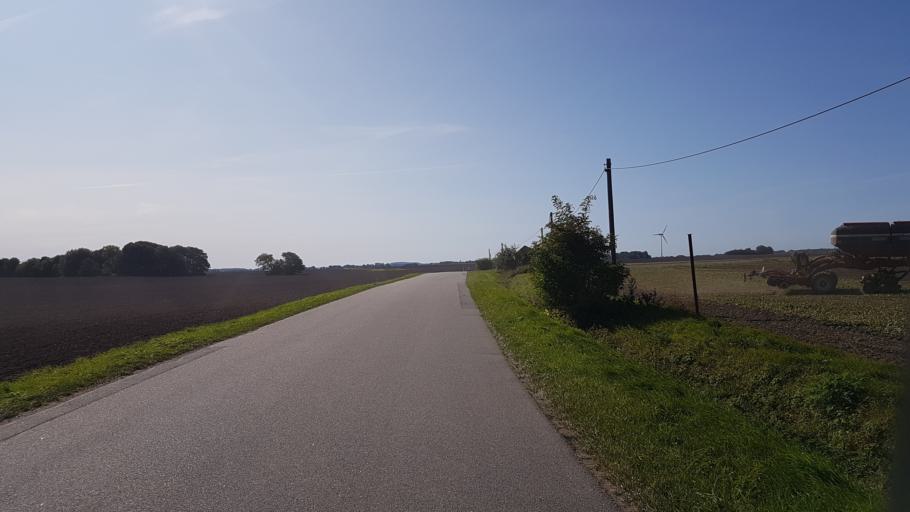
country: DE
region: Mecklenburg-Vorpommern
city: Altenkirchen
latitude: 54.6607
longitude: 13.3451
